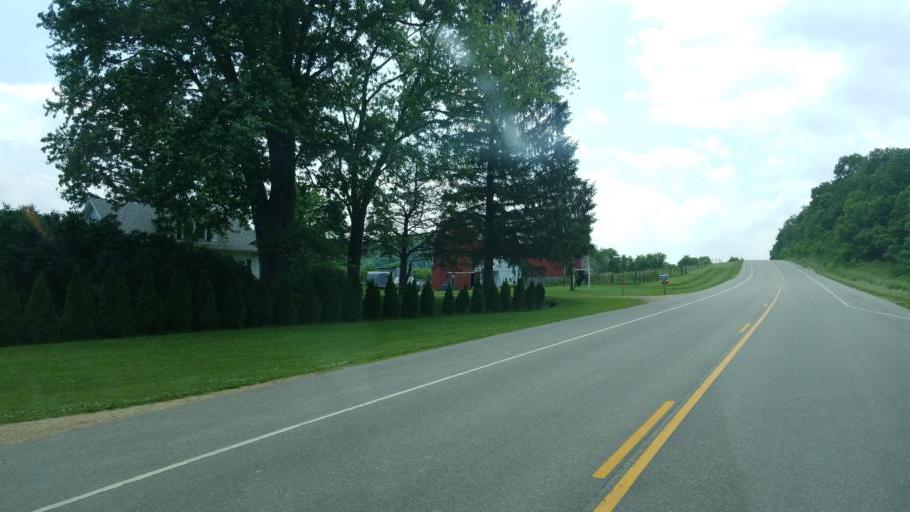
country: US
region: Wisconsin
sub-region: Vernon County
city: Viroqua
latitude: 43.4718
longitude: -90.6981
